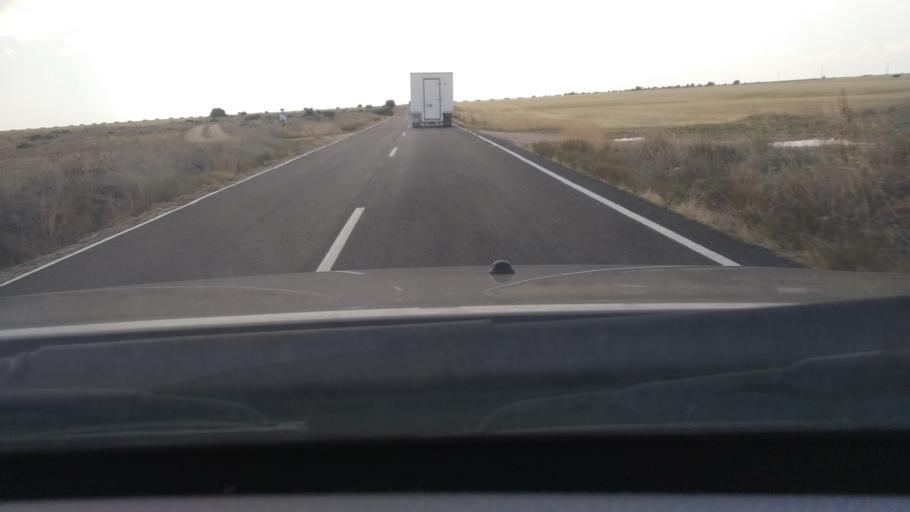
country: ES
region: Castille and Leon
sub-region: Provincia de Burgos
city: Iglesiarrubia
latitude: 41.9548
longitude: -3.8285
